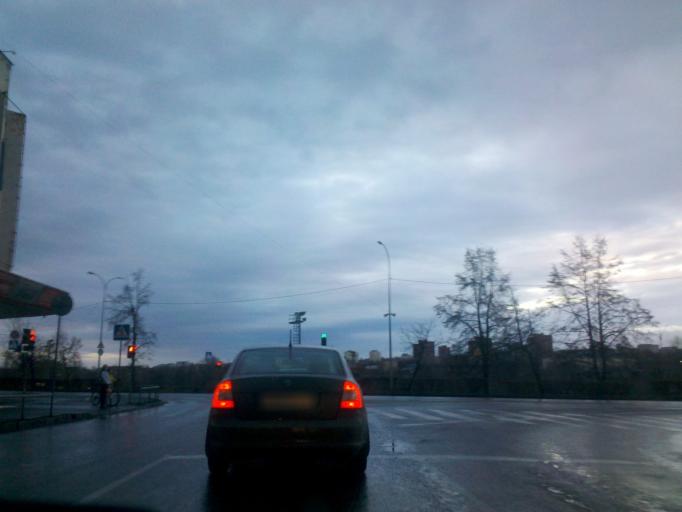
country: RU
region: Republic of Karelia
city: Petrozavodsk
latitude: 61.7883
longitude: 34.3748
